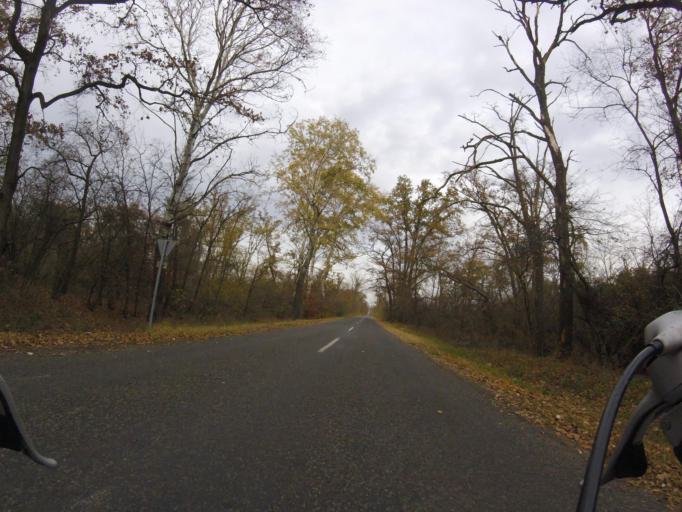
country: HU
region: Pest
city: Csemo
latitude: 47.0822
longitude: 19.6690
